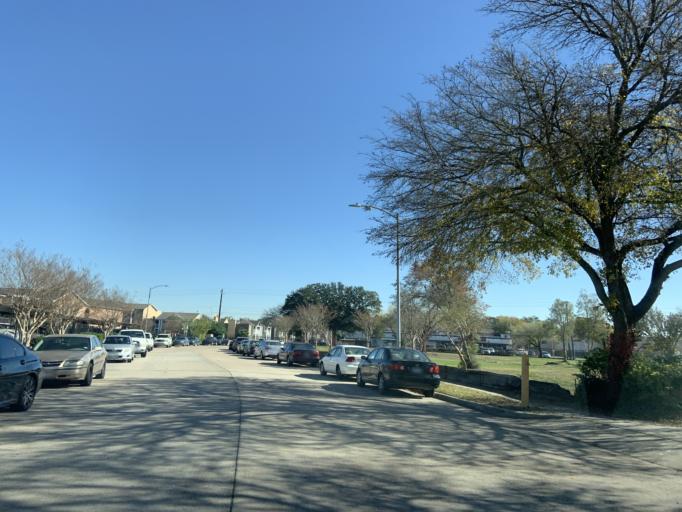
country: US
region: Texas
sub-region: Harris County
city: Bellaire
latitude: 29.6784
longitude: -95.5100
